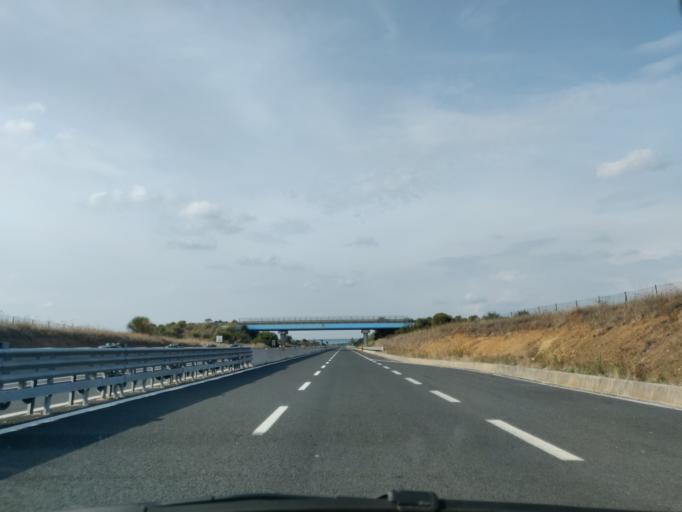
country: IT
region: Latium
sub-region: Provincia di Viterbo
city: Blera
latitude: 42.3400
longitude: 11.9835
